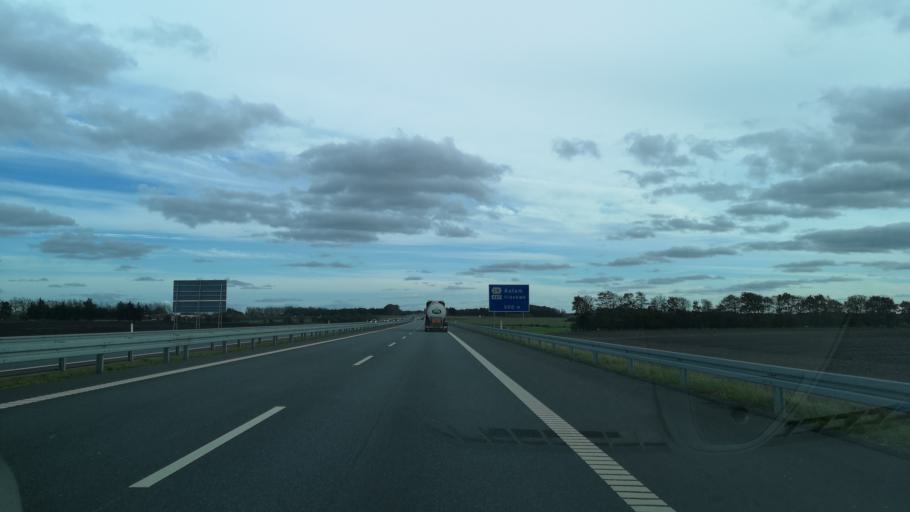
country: DK
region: Central Jutland
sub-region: Herning Kommune
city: Avlum
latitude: 56.2617
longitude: 8.7685
